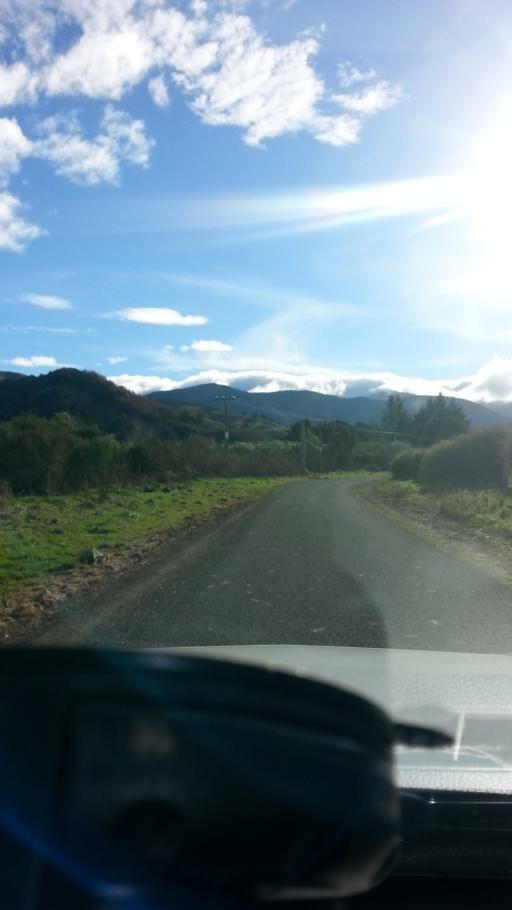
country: NZ
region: Wellington
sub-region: Masterton District
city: Masterton
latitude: -40.8951
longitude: 175.5346
